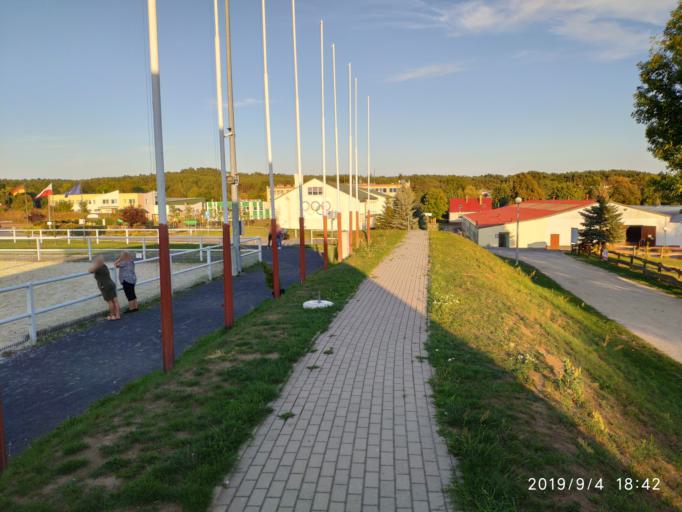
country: PL
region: Lubusz
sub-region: Zielona Gora
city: Zielona Gora
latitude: 51.8978
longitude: 15.5665
